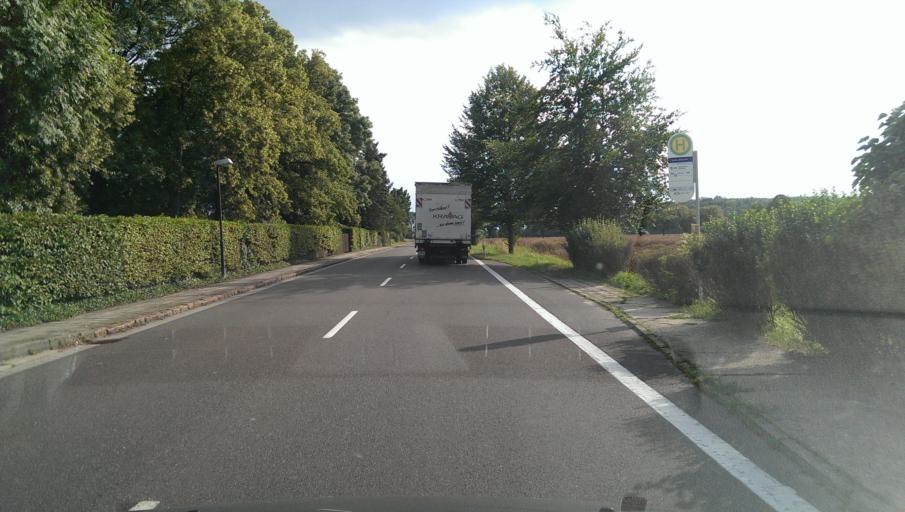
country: DE
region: Saxony
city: Elstertrebnitz
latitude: 51.1272
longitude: 12.2133
